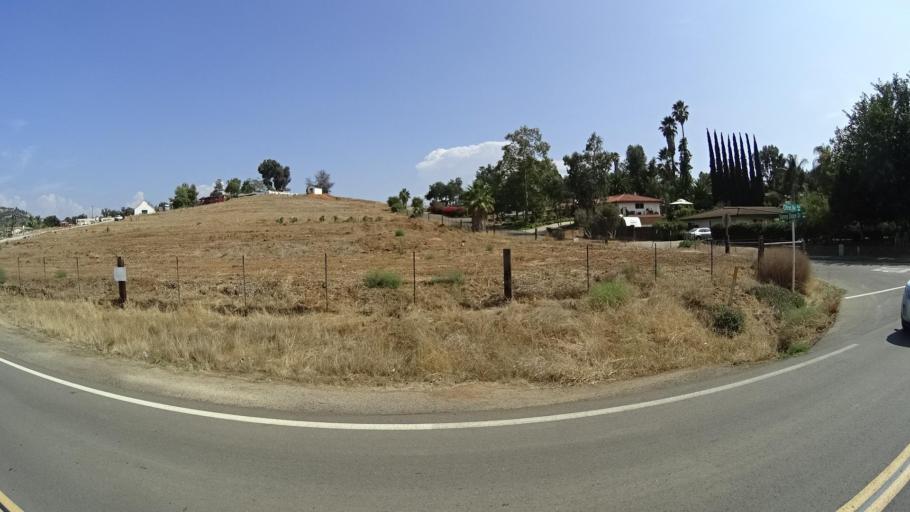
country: US
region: California
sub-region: San Diego County
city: Escondido
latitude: 33.1122
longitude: -117.0465
